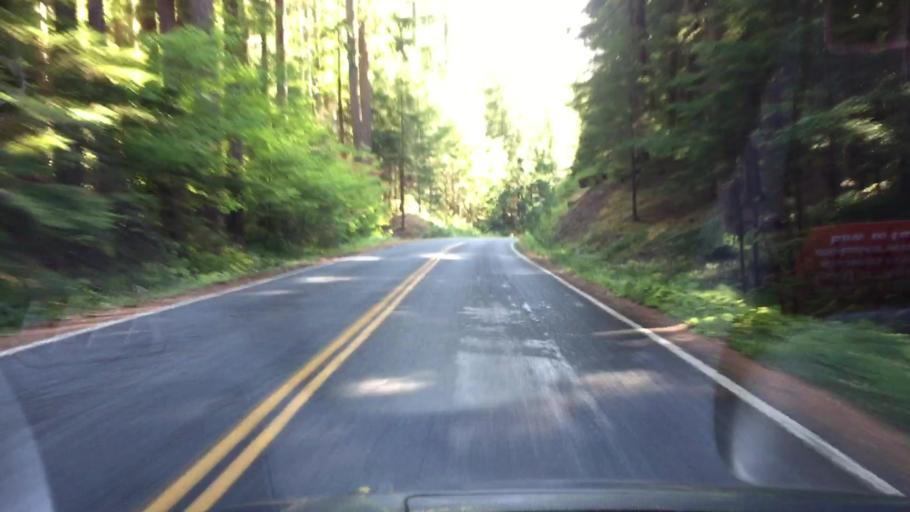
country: US
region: Washington
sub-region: Pierce County
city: Buckley
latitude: 46.7299
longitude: -121.5702
